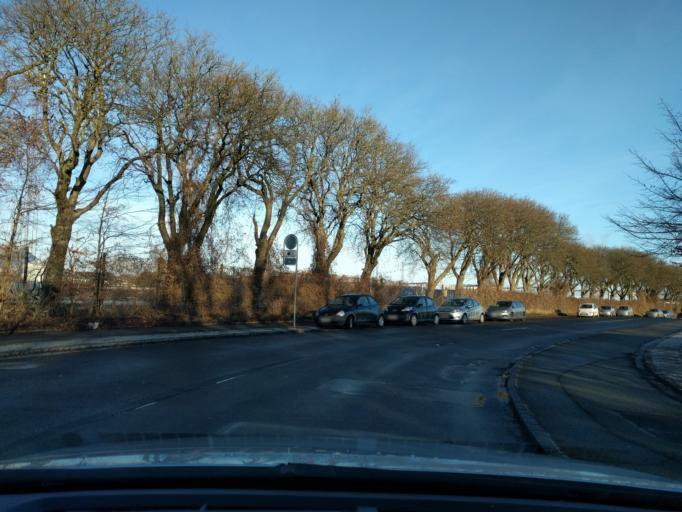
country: DK
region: South Denmark
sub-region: Odense Kommune
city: Odense
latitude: 55.3998
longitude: 10.3753
